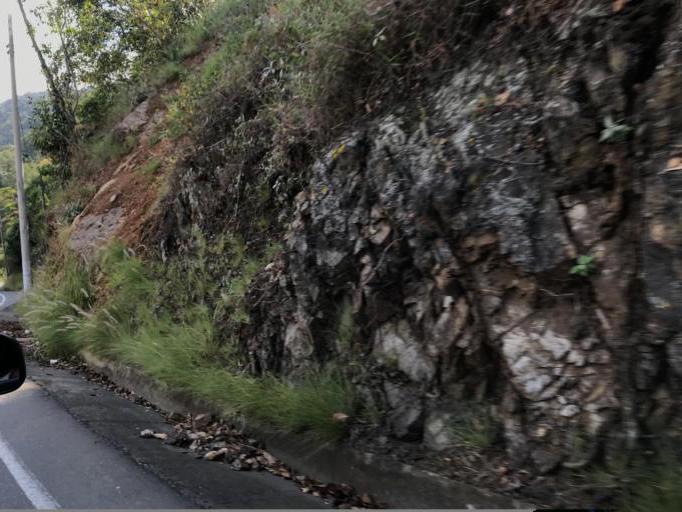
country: CO
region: Valle del Cauca
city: Cali
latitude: 3.4844
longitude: -76.6021
